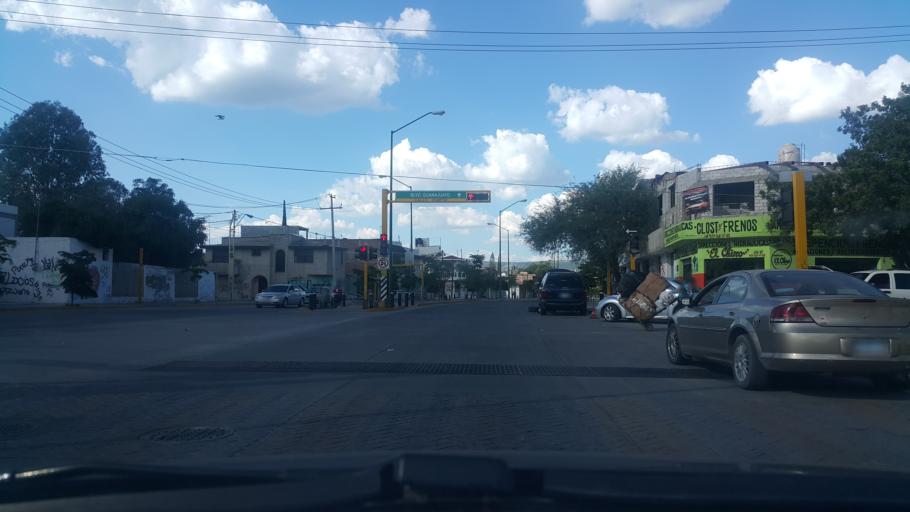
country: MX
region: Guanajuato
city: Leon
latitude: 21.1346
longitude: -101.6516
